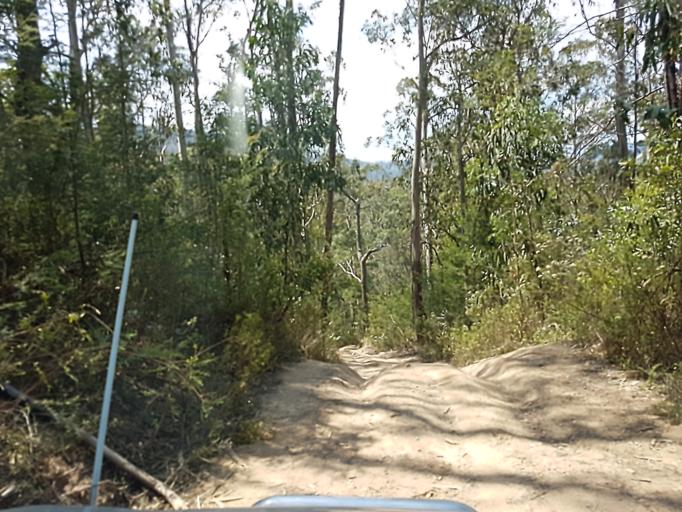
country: AU
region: Victoria
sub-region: East Gippsland
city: Lakes Entrance
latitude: -37.4024
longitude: 148.3174
